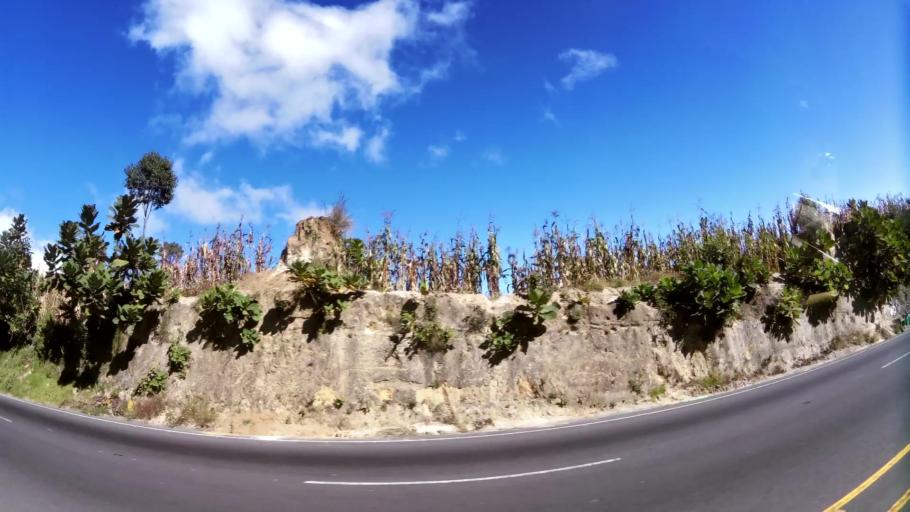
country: GT
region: Solola
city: Santa Catarina Ixtahuacan
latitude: 14.8210
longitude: -91.3381
